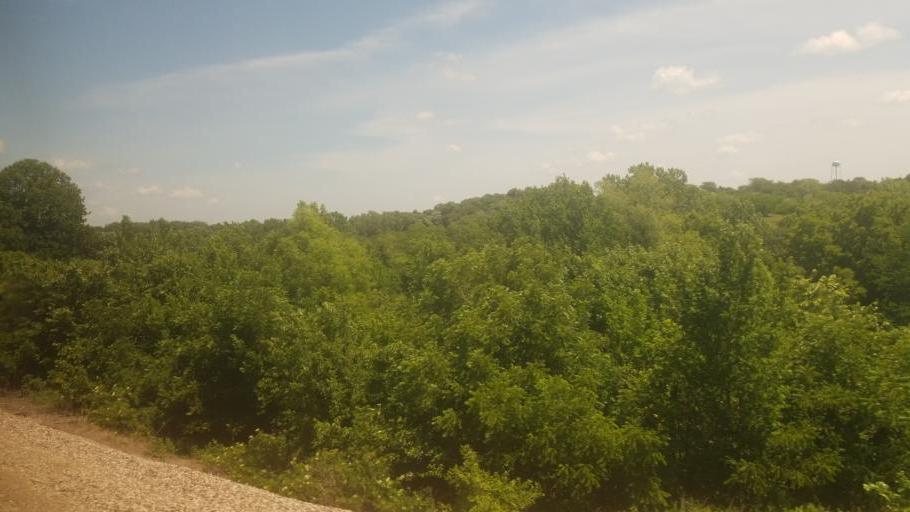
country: US
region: Missouri
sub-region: Linn County
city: Marceline
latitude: 39.8367
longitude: -92.8227
